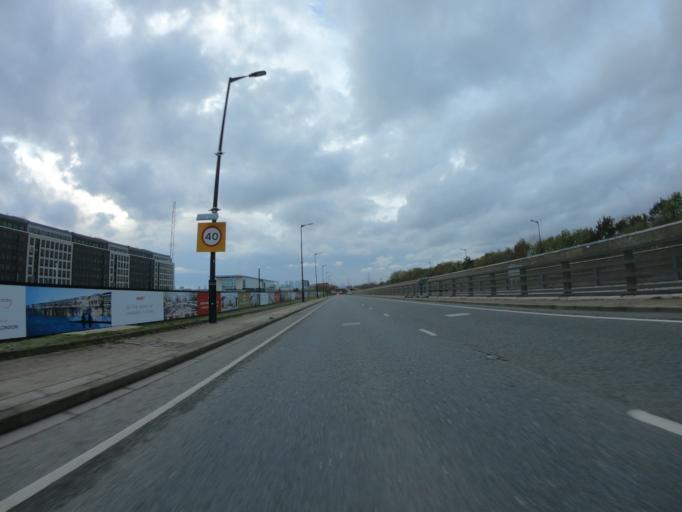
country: GB
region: England
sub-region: Greater London
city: Woolwich
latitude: 51.5089
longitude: 0.0521
